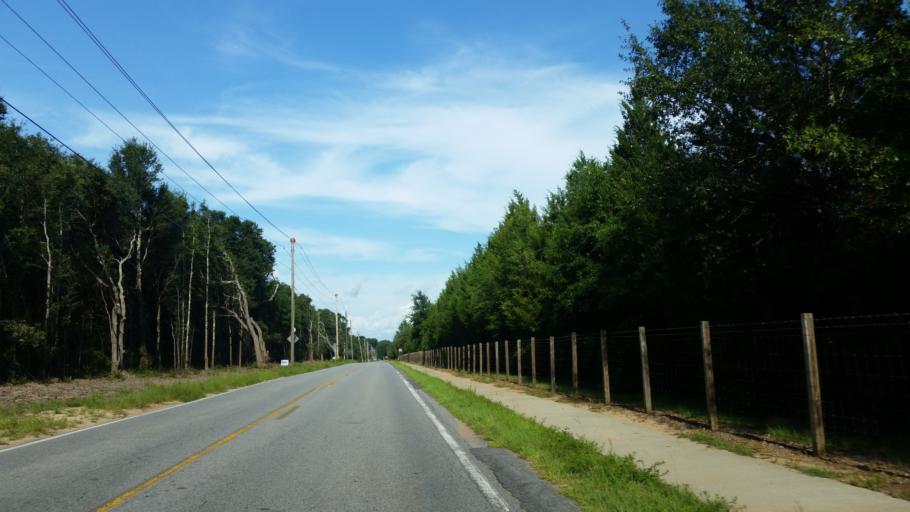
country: US
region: Florida
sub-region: Santa Rosa County
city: Pace
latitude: 30.6326
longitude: -87.1466
